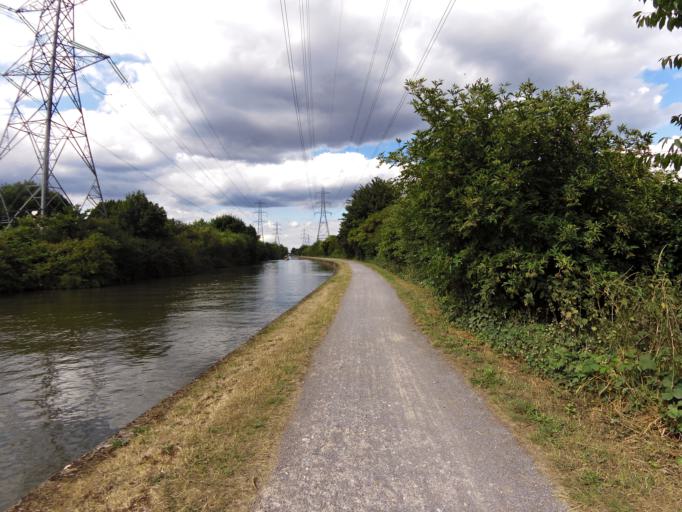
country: GB
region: England
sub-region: Greater London
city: Walthamstow
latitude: 51.6311
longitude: -0.0304
